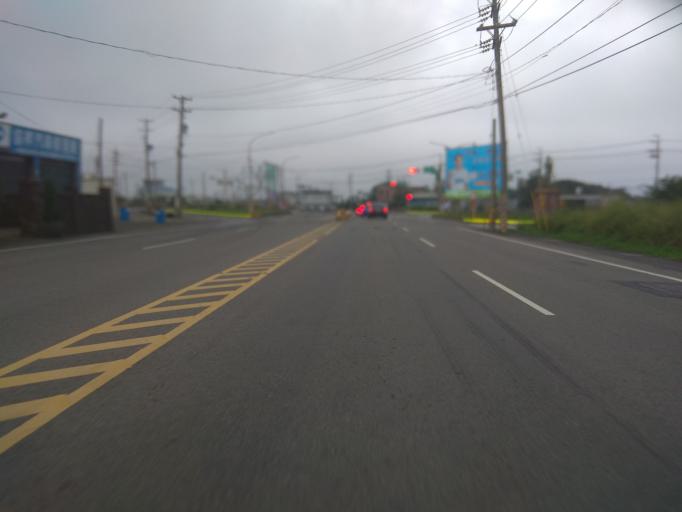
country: TW
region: Taiwan
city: Taoyuan City
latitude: 25.0334
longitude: 121.0957
